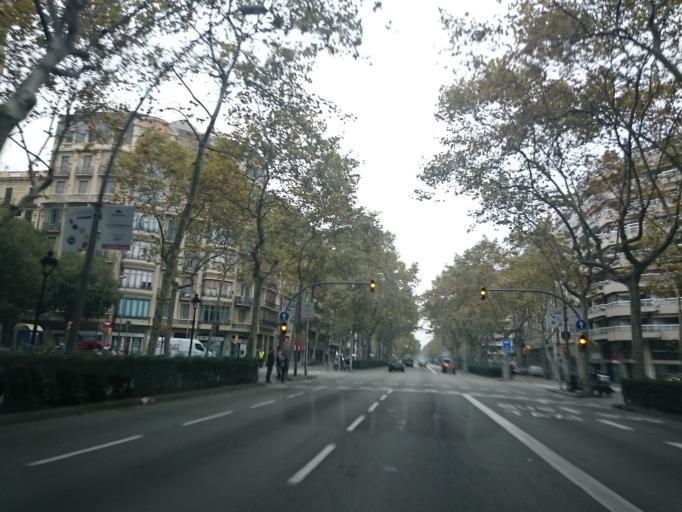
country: ES
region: Catalonia
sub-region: Provincia de Barcelona
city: Barcelona
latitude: 41.3809
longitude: 2.1570
